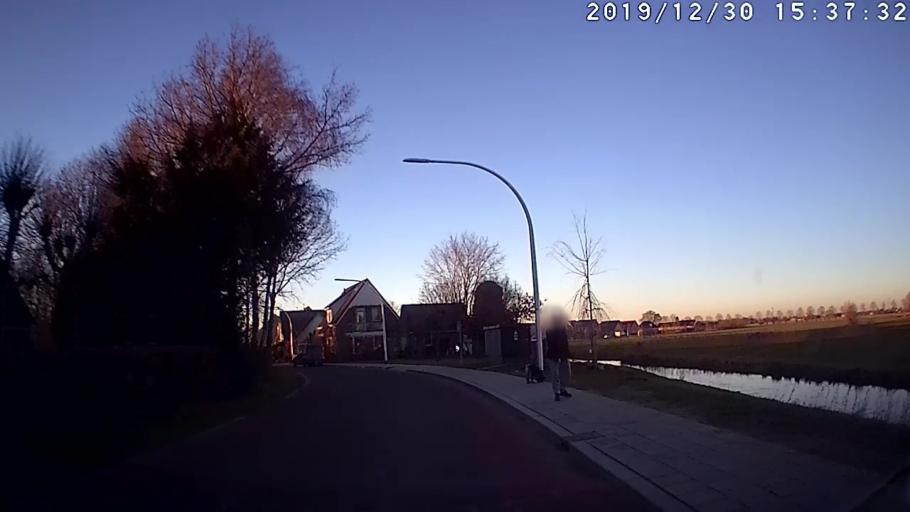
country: NL
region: Overijssel
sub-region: Gemeente Raalte
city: Heino
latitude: 52.4577
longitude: 6.1771
